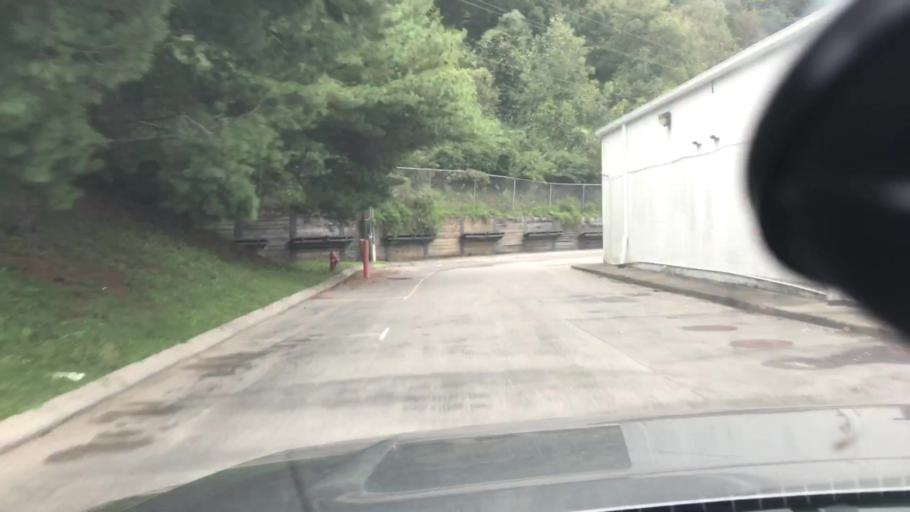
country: US
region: Tennessee
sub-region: Davidson County
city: Belle Meade
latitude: 36.0739
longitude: -86.9177
